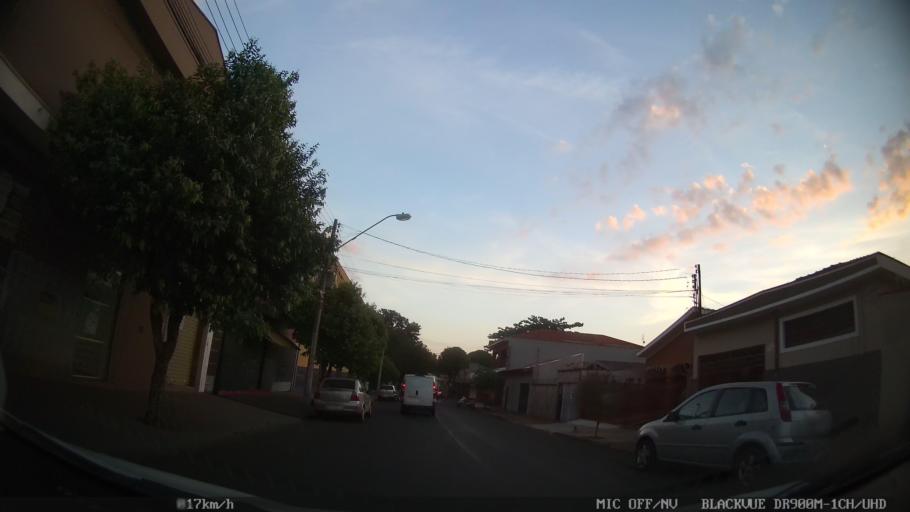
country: BR
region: Sao Paulo
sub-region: Ribeirao Preto
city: Ribeirao Preto
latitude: -21.1562
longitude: -47.8315
